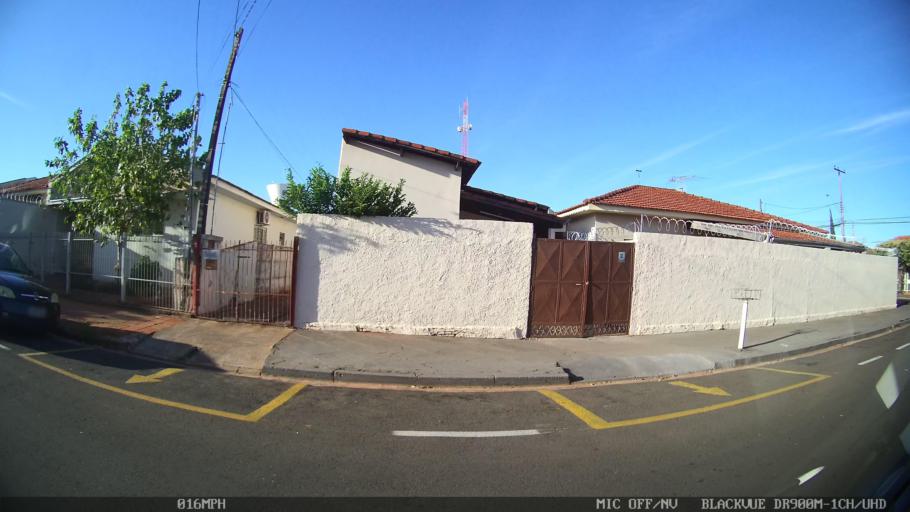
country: BR
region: Sao Paulo
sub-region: Sao Jose Do Rio Preto
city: Sao Jose do Rio Preto
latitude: -20.8311
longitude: -49.3735
